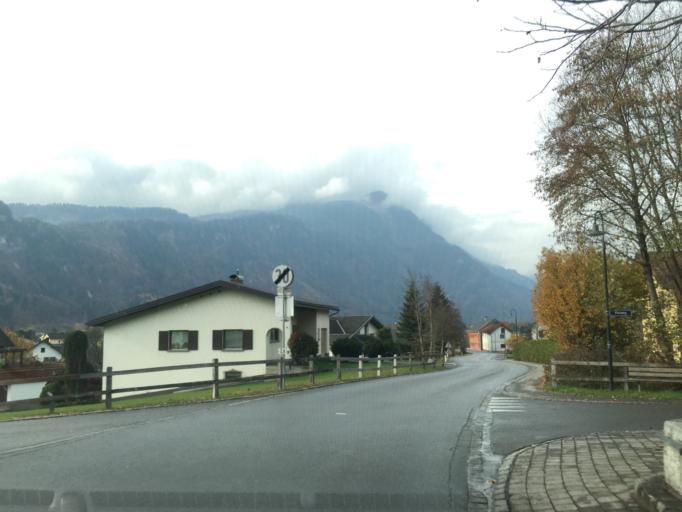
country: AT
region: Vorarlberg
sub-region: Politischer Bezirk Bludenz
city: Nuziders
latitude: 47.1738
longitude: 9.7975
